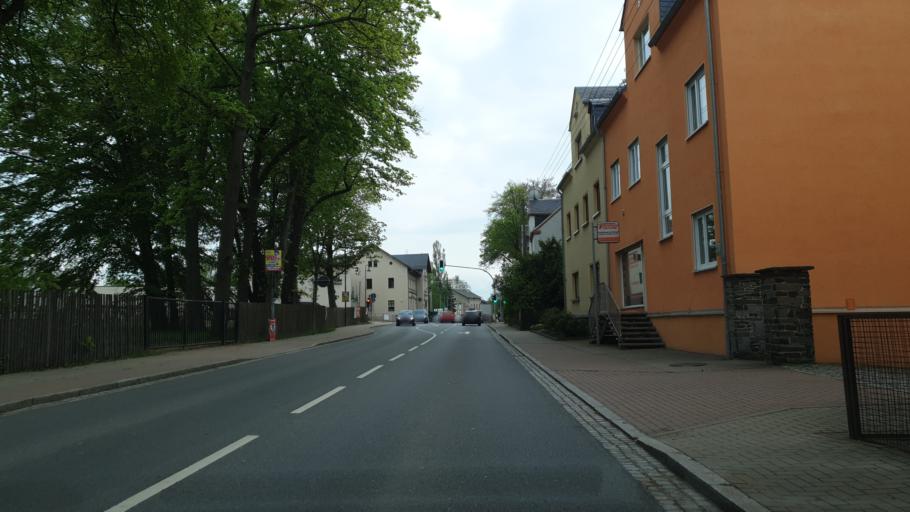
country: DE
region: Saxony
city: Lugau
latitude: 50.7428
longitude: 12.7467
